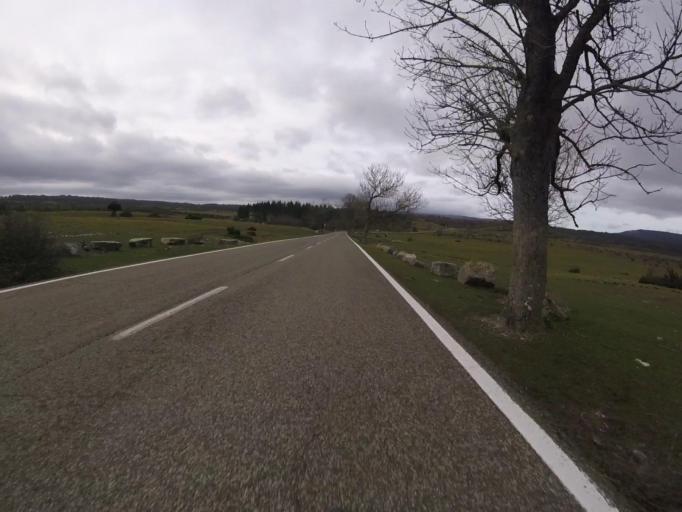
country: ES
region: Navarre
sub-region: Provincia de Navarra
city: Eulate
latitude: 42.8102
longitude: -2.1576
